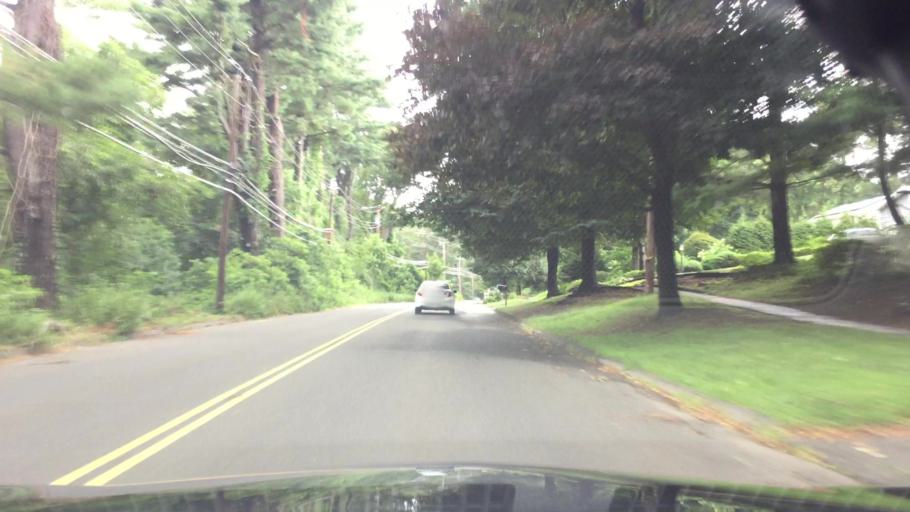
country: US
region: Connecticut
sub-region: Fairfield County
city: Stratford
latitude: 41.2468
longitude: -73.1218
